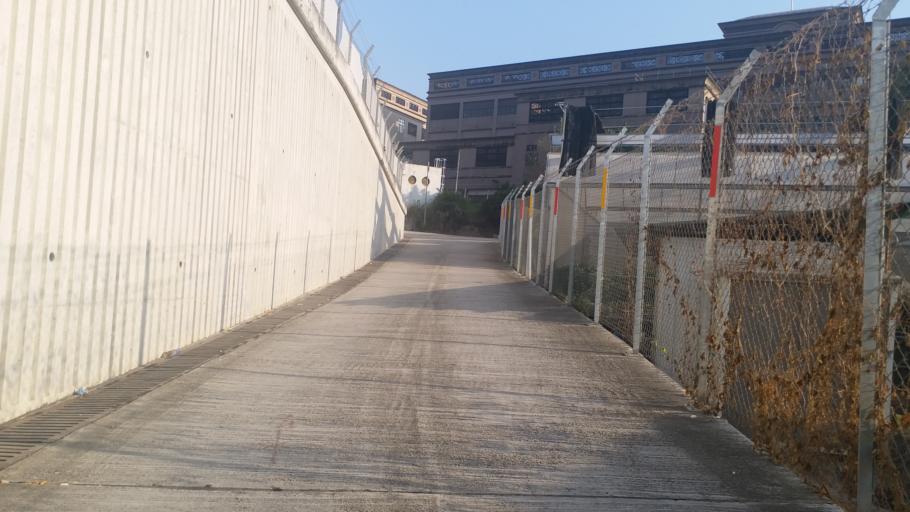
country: HK
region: Tuen Mun
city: Tuen Mun
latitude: 22.4107
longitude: 113.9723
